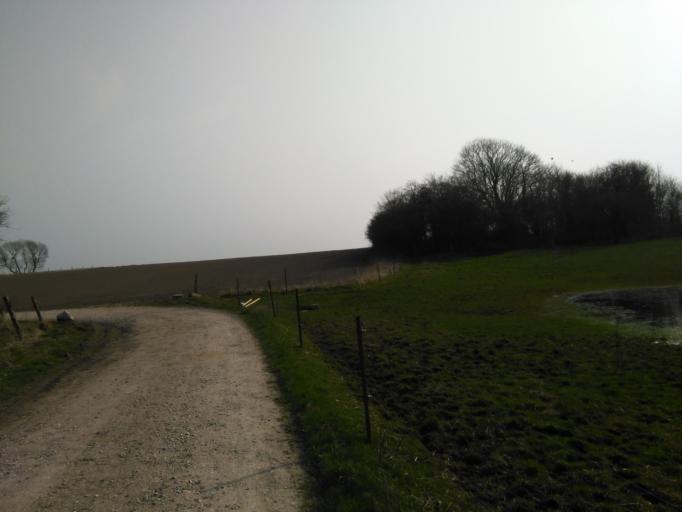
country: DK
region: Central Jutland
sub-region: Arhus Kommune
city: Beder
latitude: 56.0640
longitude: 10.2262
